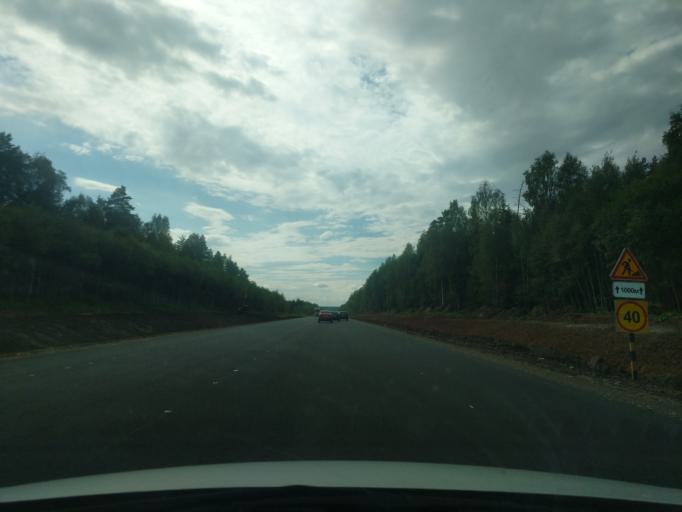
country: RU
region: Kostroma
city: Sudislavl'
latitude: 57.8246
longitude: 41.4985
